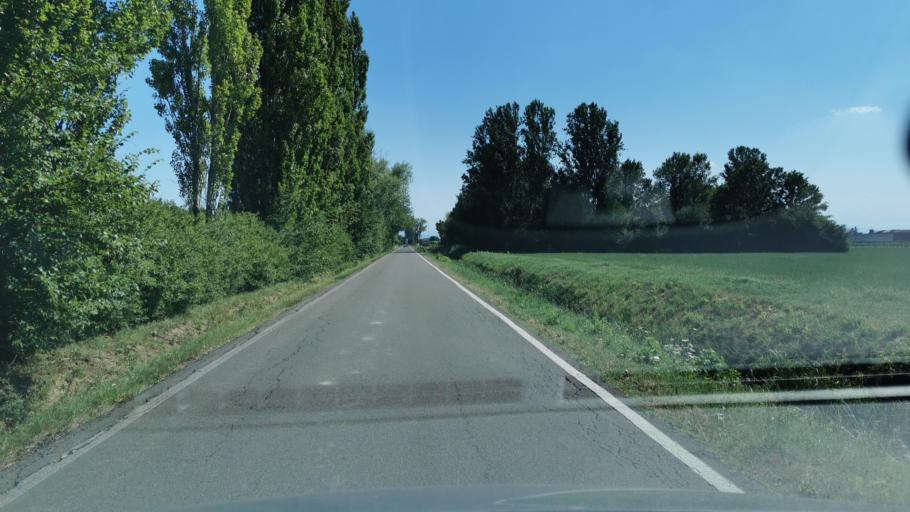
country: IT
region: Emilia-Romagna
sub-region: Provincia di Modena
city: Limidi
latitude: 44.7749
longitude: 10.9178
